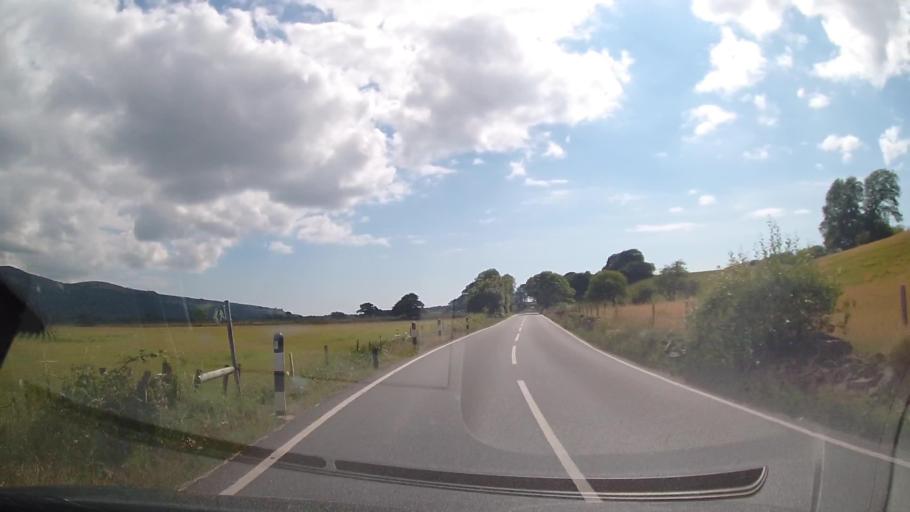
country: GB
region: Wales
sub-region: Gwynedd
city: Penrhyndeudraeth
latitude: 52.8904
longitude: -4.0935
